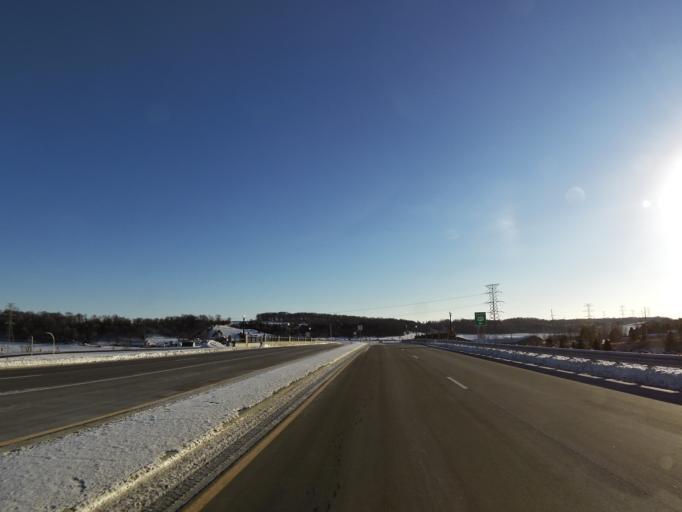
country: US
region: Minnesota
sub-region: Scott County
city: Shakopee
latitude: 44.7791
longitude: -93.5598
